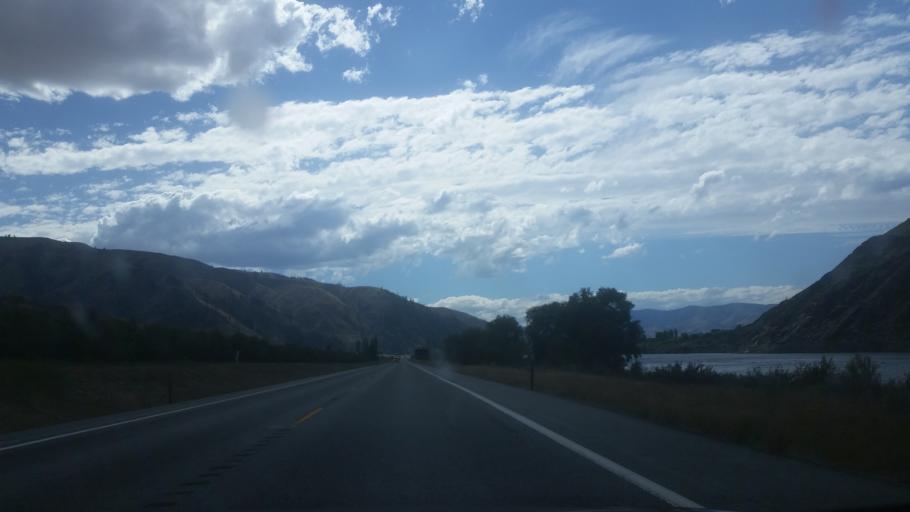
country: US
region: Washington
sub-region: Chelan County
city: Chelan
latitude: 47.7720
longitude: -120.0438
